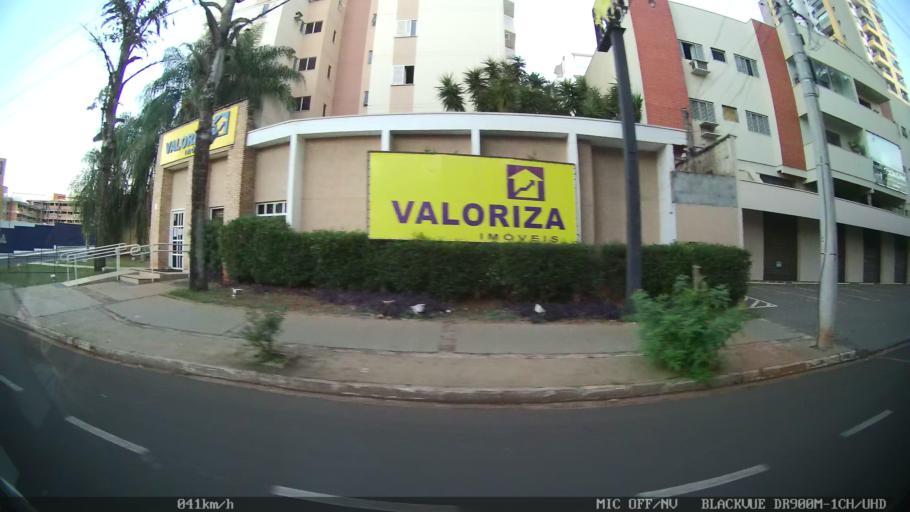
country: BR
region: Sao Paulo
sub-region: Sao Jose Do Rio Preto
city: Sao Jose do Rio Preto
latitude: -20.8320
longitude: -49.3910
